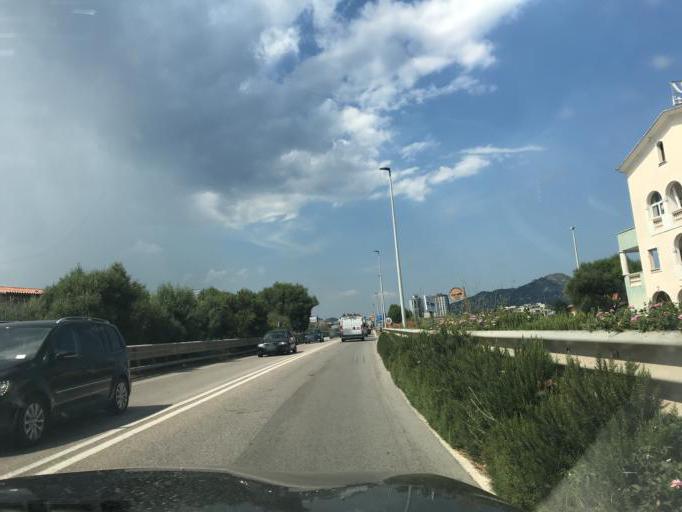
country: IT
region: Sardinia
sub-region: Provincia di Olbia-Tempio
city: Olbia
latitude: 40.9141
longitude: 9.5017
